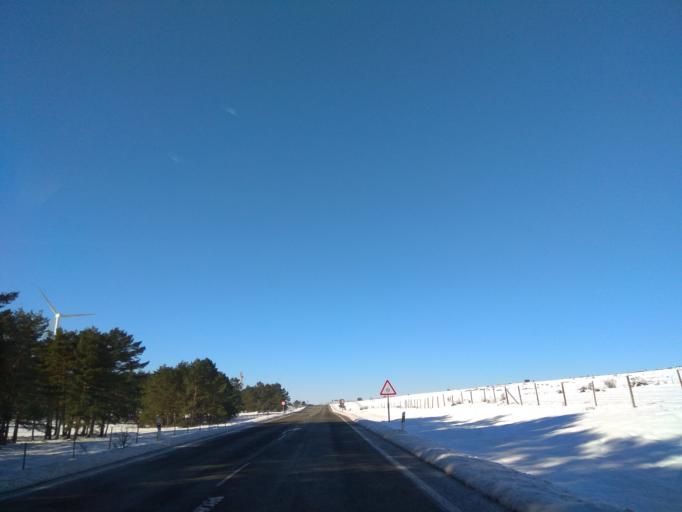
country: ES
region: Castille and Leon
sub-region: Provincia de Burgos
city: Medina de Pomar
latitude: 42.9305
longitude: -3.6523
